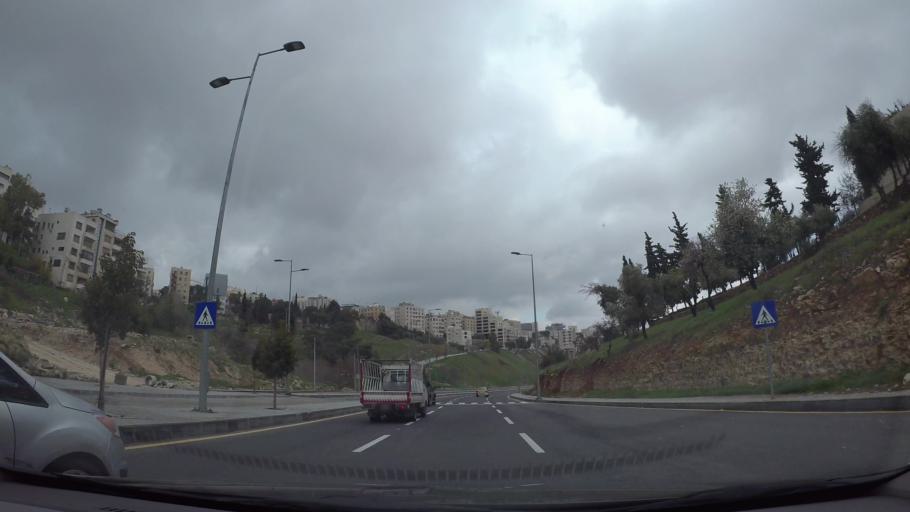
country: JO
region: Amman
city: Amman
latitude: 31.9517
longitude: 35.8969
